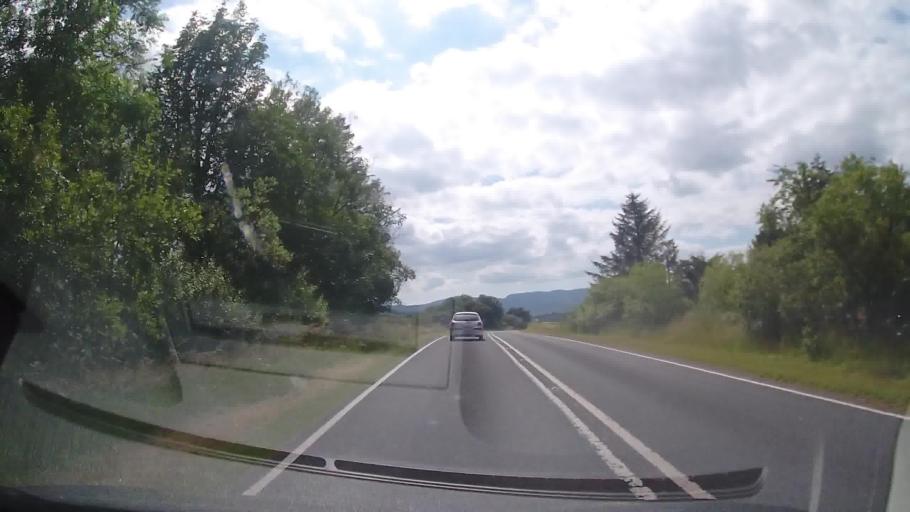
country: GB
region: Wales
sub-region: Gwynedd
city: Trawsfynydd
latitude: 52.9087
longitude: -3.8559
